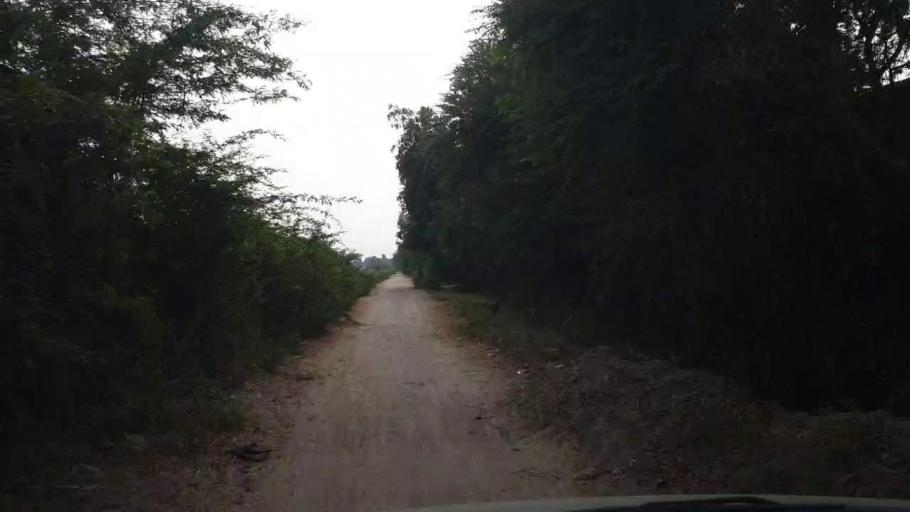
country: PK
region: Sindh
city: Matli
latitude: 25.0032
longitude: 68.7013
